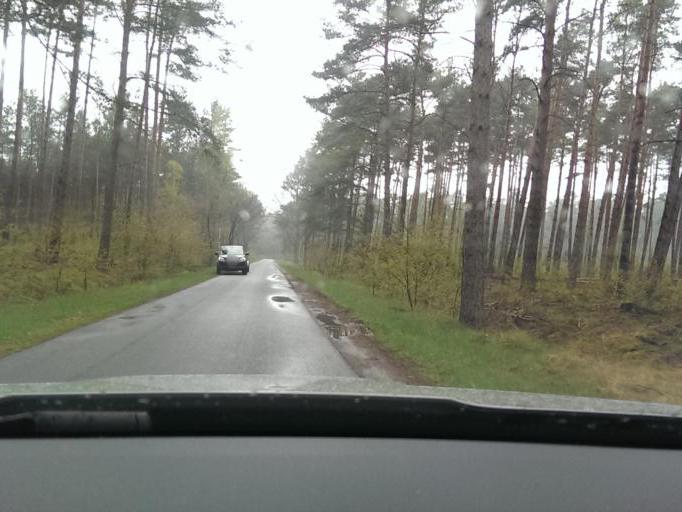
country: DE
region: Lower Saxony
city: Elze
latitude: 52.5969
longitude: 9.7769
